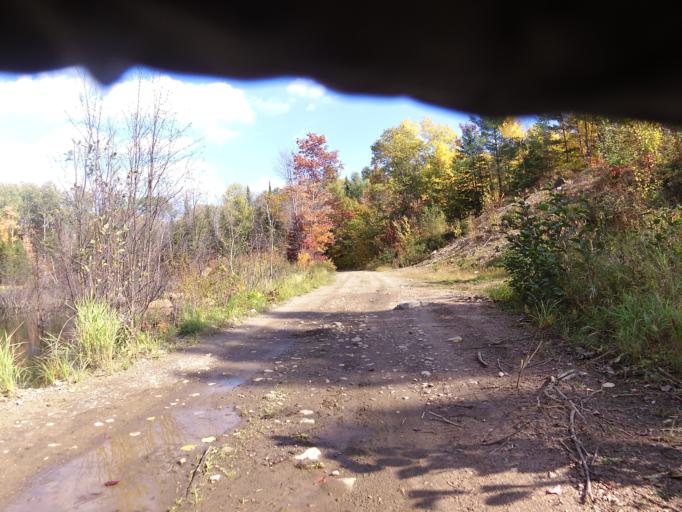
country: CA
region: Ontario
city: Petawawa
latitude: 45.8006
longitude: -77.3081
